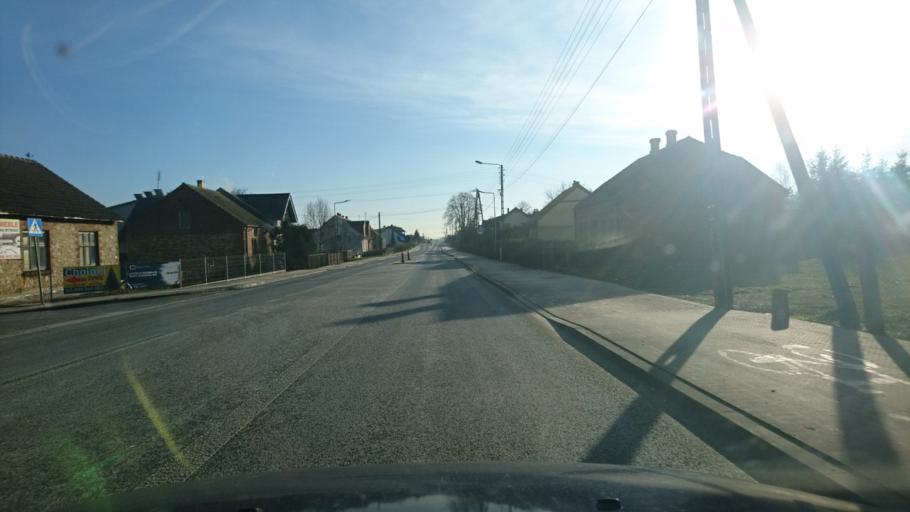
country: PL
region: Silesian Voivodeship
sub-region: Powiat klobucki
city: Starokrzepice
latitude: 51.0170
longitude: 18.6534
